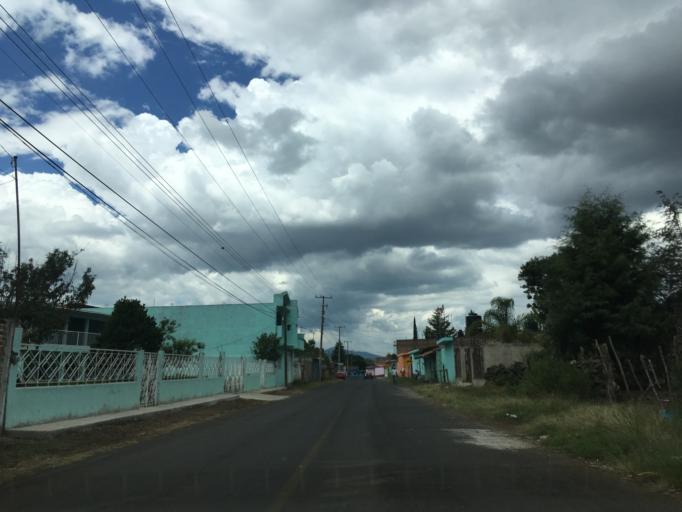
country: MX
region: Michoacan
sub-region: Jimenez
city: Copandaro (Copandaro del Cuatro)
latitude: 19.8166
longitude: -101.6800
